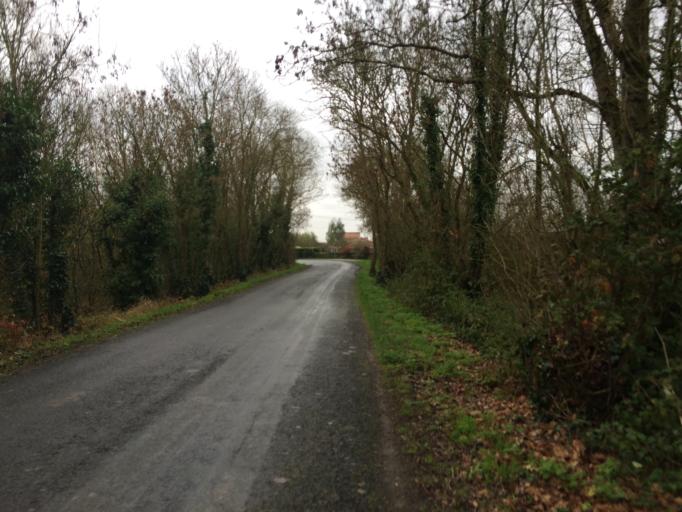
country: FR
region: Pays de la Loire
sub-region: Departement de la Vendee
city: Chaille-les-Marais
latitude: 46.3799
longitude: -1.0101
